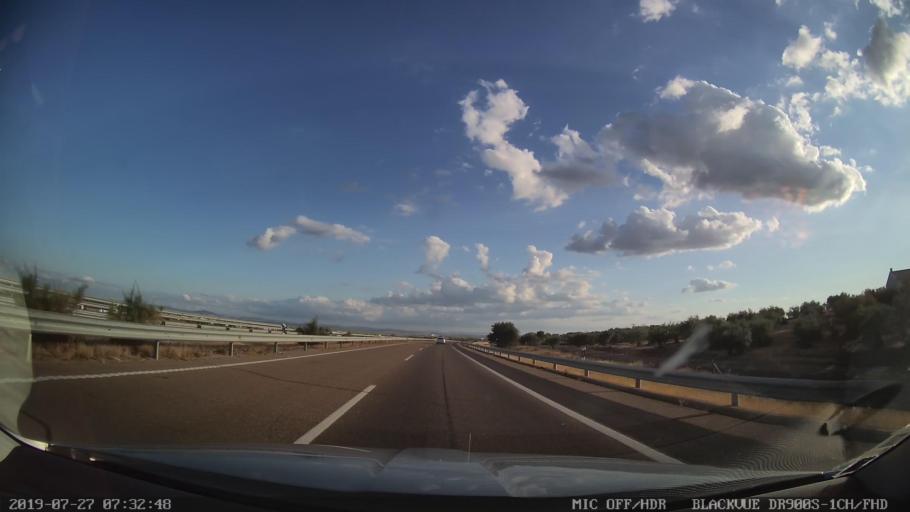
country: ES
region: Extremadura
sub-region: Provincia de Caceres
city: Miajadas
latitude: 39.1526
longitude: -5.9269
